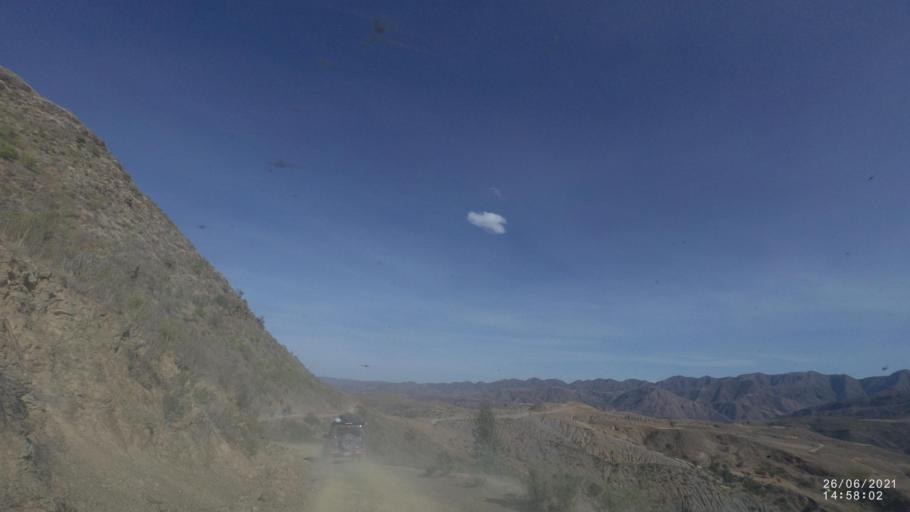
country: BO
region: Cochabamba
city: Mizque
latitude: -17.9432
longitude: -65.6200
